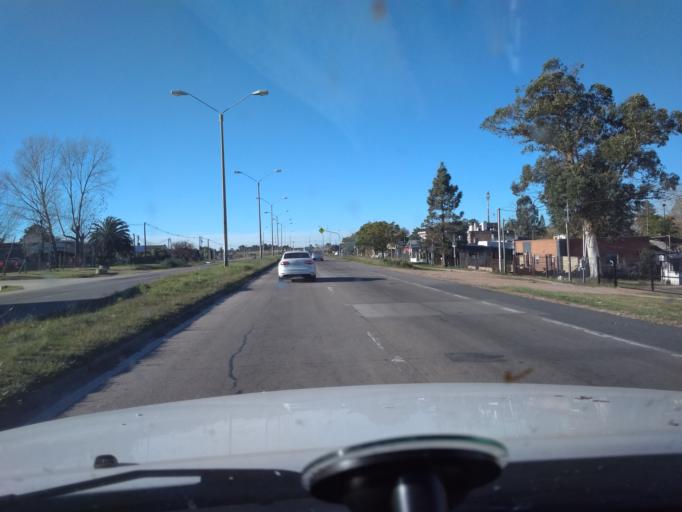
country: UY
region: Canelones
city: Colonia Nicolich
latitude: -34.7780
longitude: -56.0553
